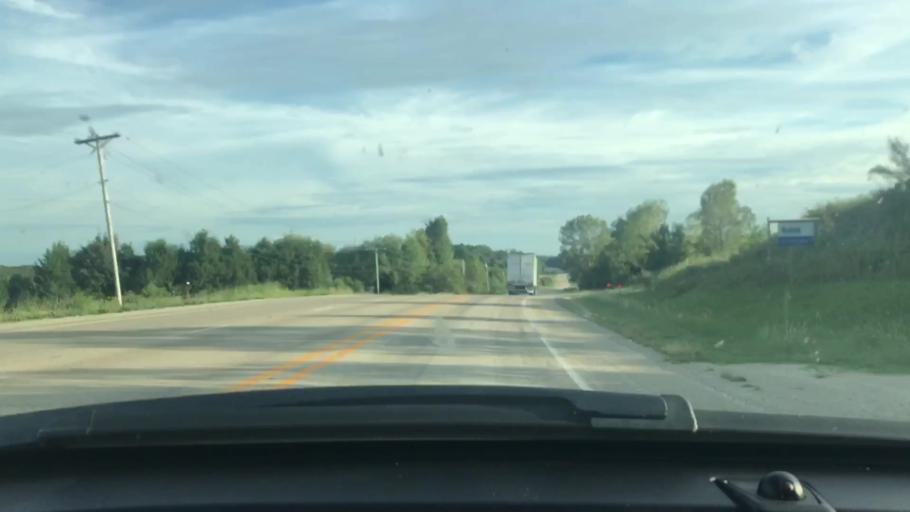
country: US
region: Arkansas
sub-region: Lawrence County
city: Hoxie
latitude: 36.1425
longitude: -91.1581
